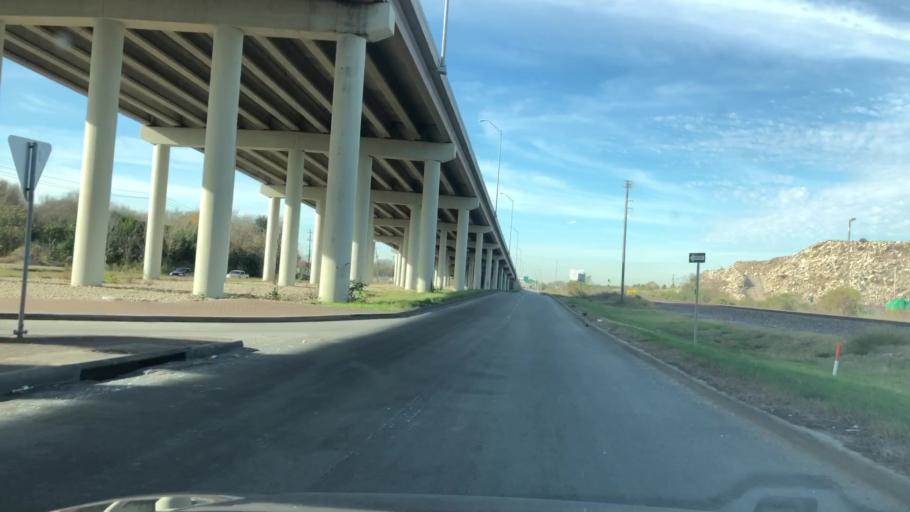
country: US
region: Texas
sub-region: Harris County
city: Bellaire
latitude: 29.6475
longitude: -95.4641
